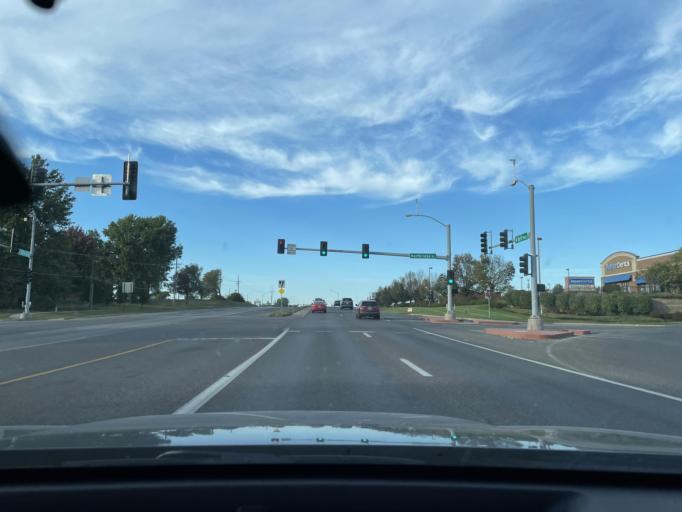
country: US
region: Missouri
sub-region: Andrew County
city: Country Club Village
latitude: 39.8107
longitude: -94.8151
